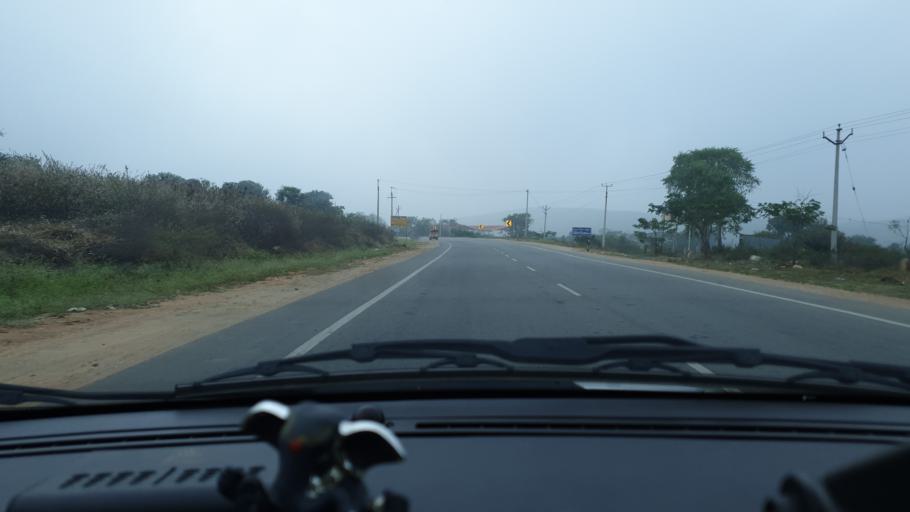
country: IN
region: Telangana
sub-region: Mahbubnagar
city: Farrukhnagar
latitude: 16.9583
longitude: 78.5132
